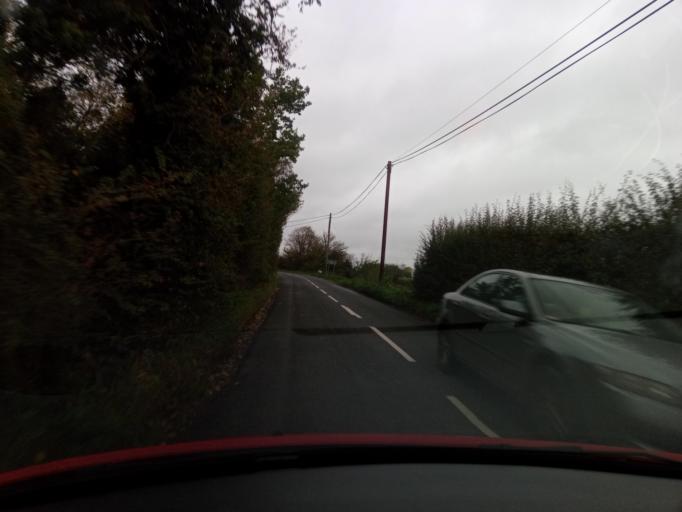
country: GB
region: England
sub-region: Essex
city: West Mersea
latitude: 51.7895
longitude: 0.9530
